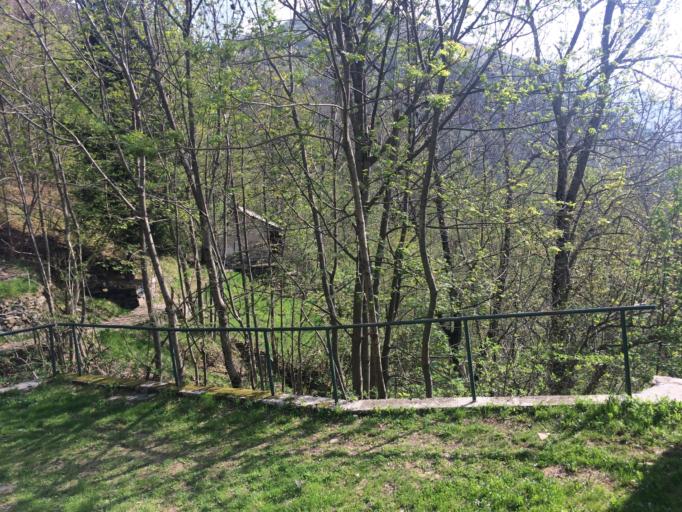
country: IT
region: Piedmont
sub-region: Provincia Verbano-Cusio-Ossola
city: Gurro
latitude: 46.0724
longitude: 8.5673
